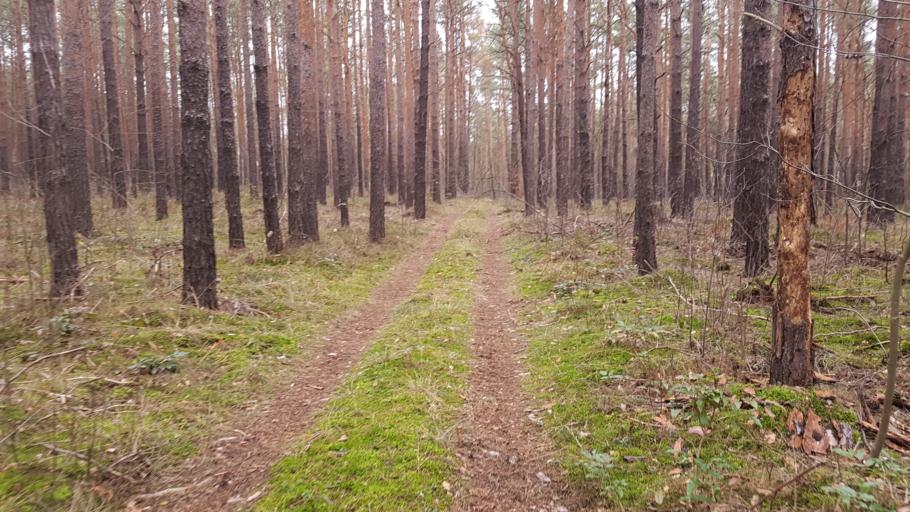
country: DE
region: Brandenburg
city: Schilda
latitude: 51.5846
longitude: 13.3959
